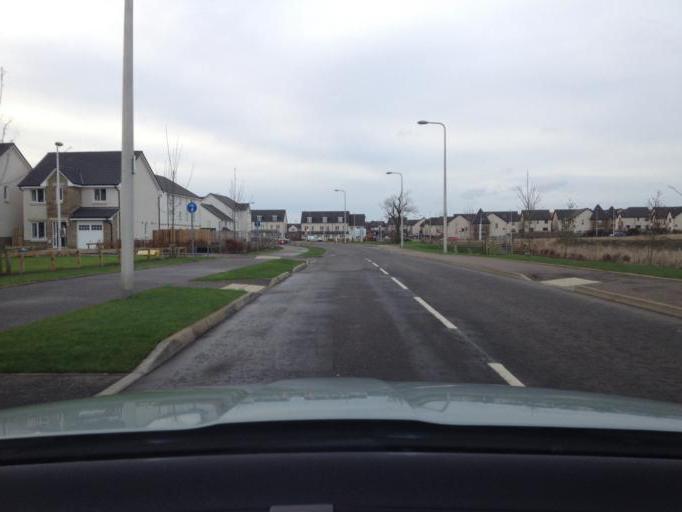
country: GB
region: Scotland
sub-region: Edinburgh
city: Kirkliston
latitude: 55.9605
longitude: -3.4005
